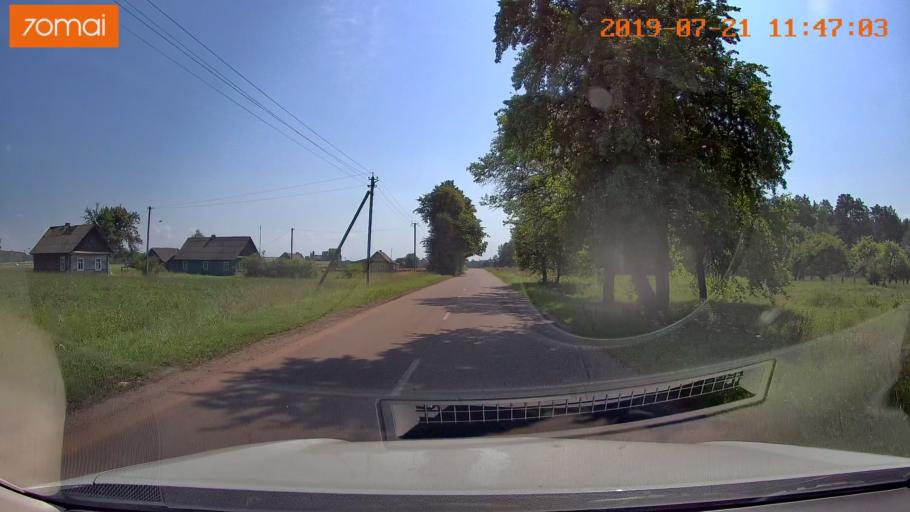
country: BY
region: Grodnenskaya
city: Lyubcha
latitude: 53.9046
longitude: 26.0405
